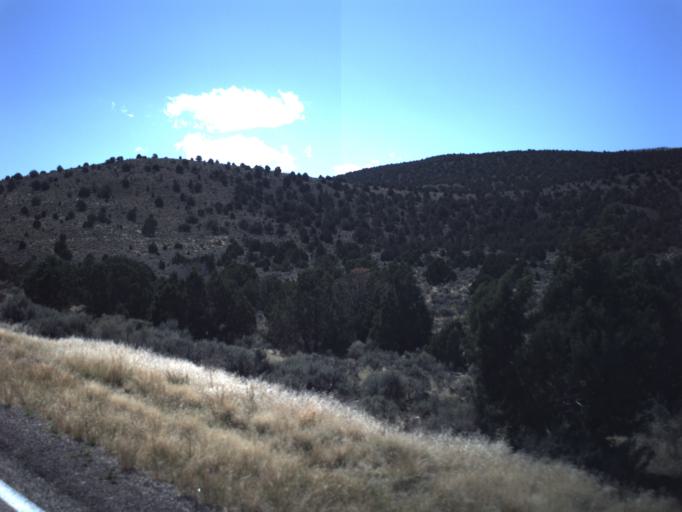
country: US
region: Utah
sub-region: Beaver County
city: Milford
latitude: 38.1270
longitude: -112.9569
